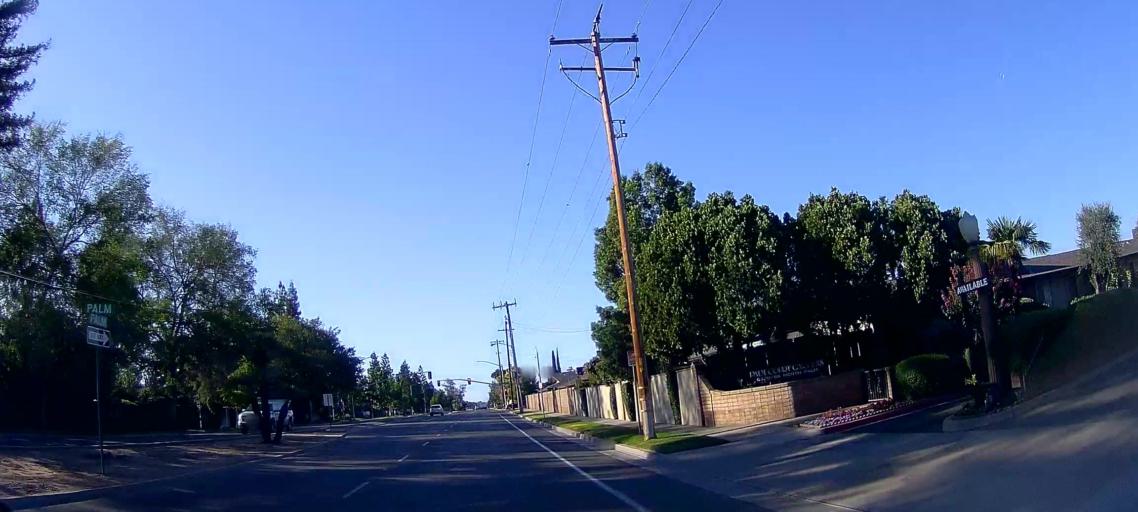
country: US
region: California
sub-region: Fresno County
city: Fresno
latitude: 36.8291
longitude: -119.8082
